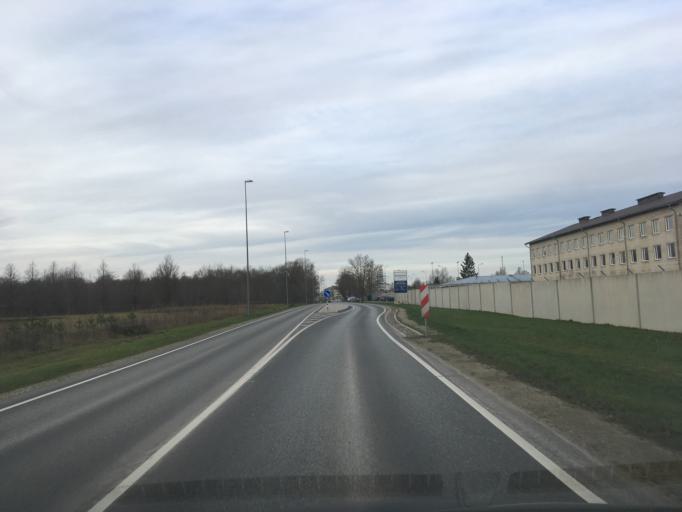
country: EE
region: Ida-Virumaa
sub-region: Johvi vald
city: Johvi
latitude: 59.3479
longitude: 27.4355
